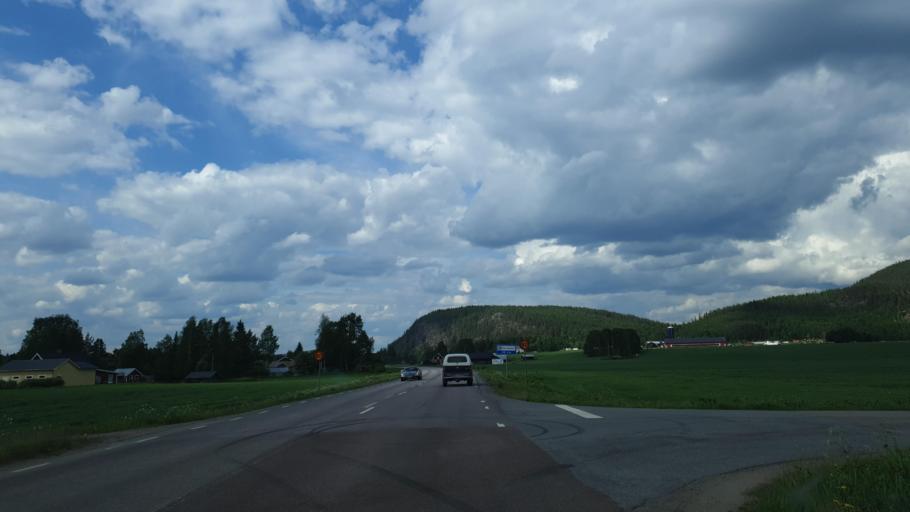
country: SE
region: Norrbotten
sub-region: Alvsbyns Kommun
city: AElvsbyn
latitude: 65.6696
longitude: 21.0466
